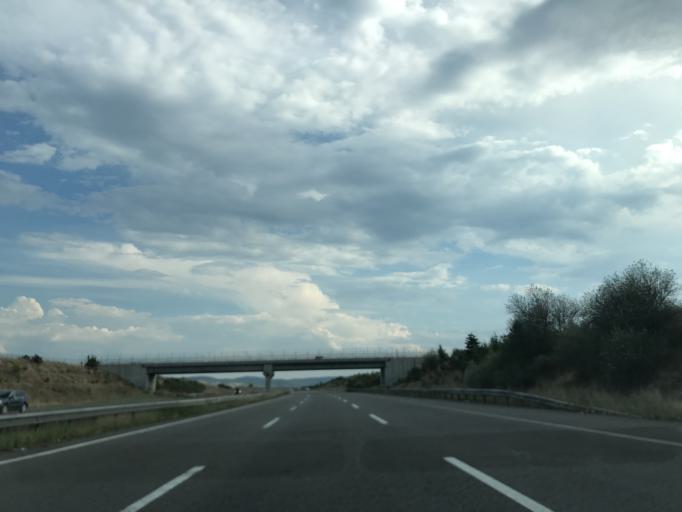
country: TR
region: Bolu
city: Gerede
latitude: 40.6999
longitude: 32.2222
